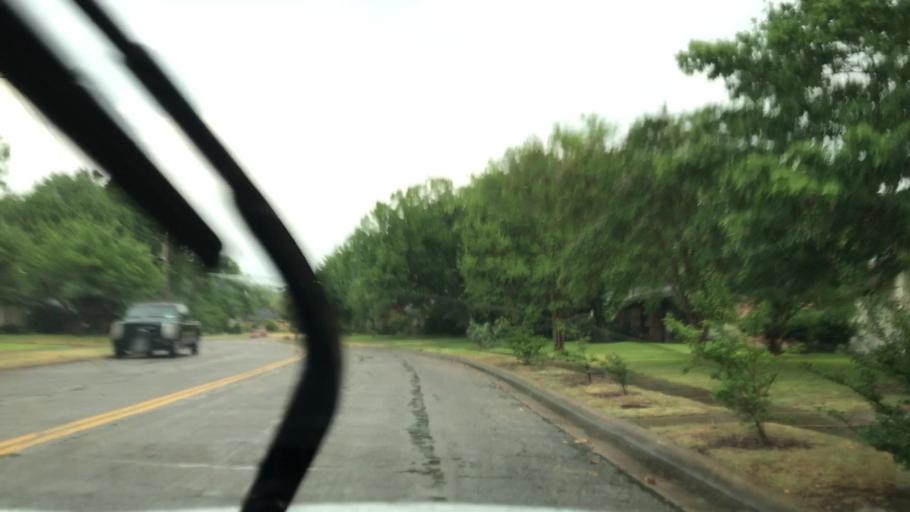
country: US
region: Texas
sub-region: Dallas County
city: Garland
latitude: 32.8728
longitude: -96.6882
